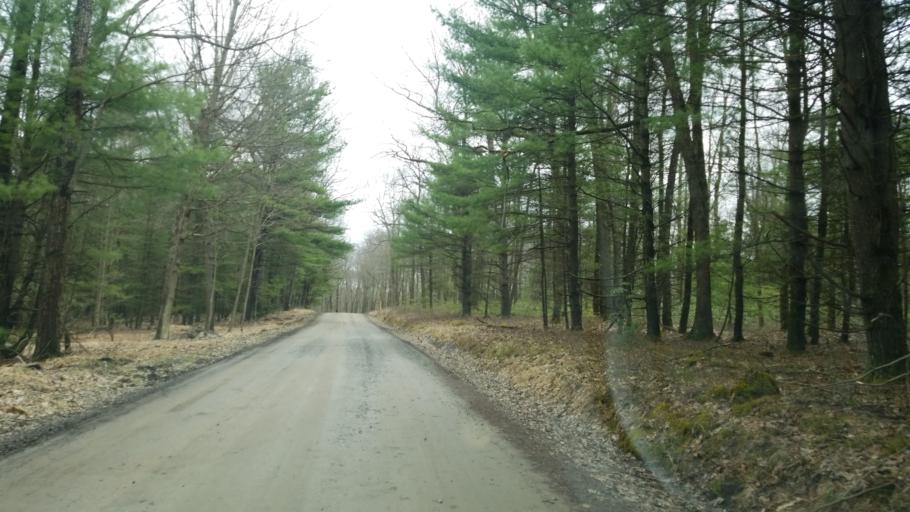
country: US
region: Pennsylvania
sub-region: Clearfield County
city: Shiloh
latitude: 41.1653
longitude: -78.2523
